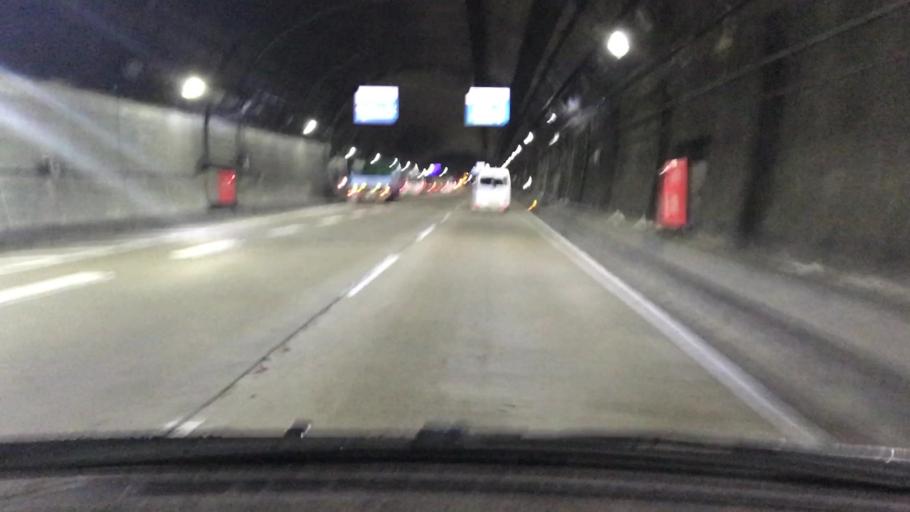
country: JP
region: Hyogo
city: Kobe
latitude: 34.7066
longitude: 135.1946
